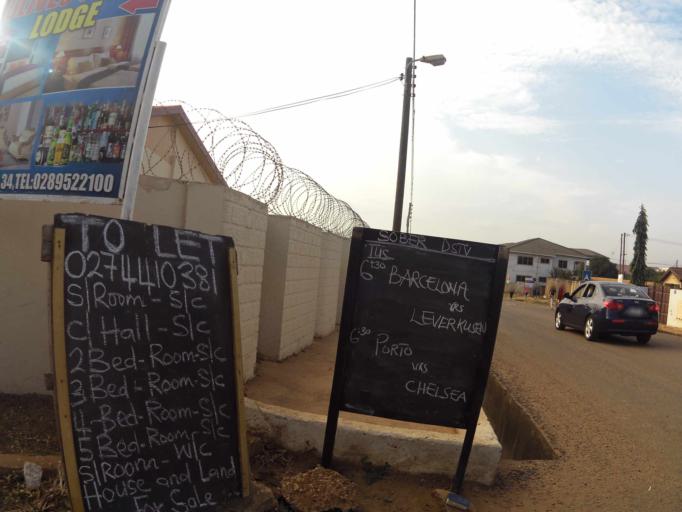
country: GH
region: Greater Accra
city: Dome
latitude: 5.6446
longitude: -0.2150
